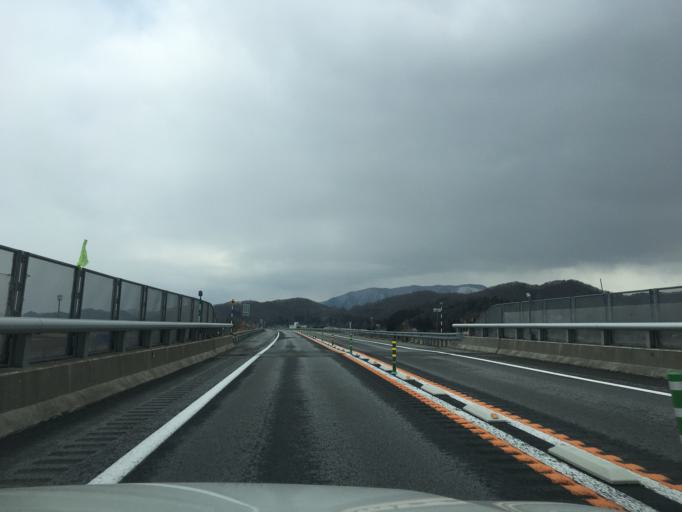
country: JP
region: Aomori
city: Aomori Shi
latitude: 40.8038
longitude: 140.7939
